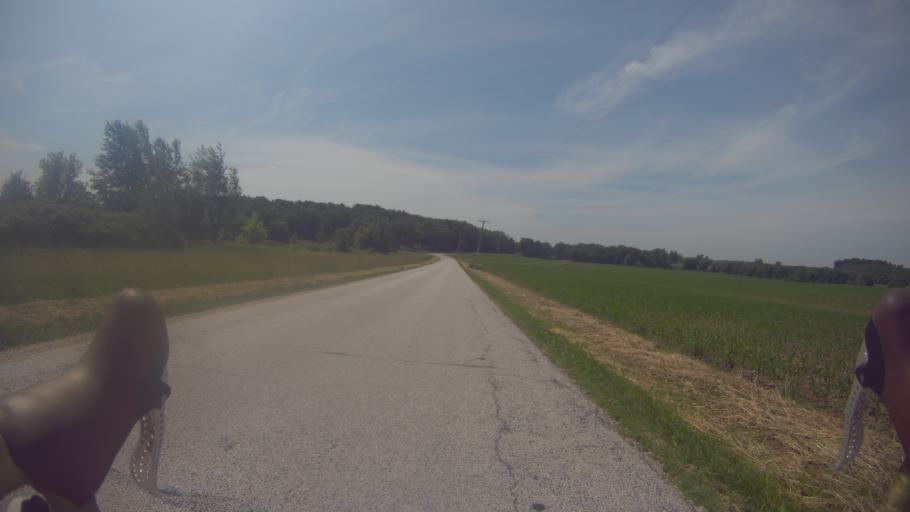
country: US
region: Wisconsin
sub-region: Jefferson County
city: Cambridge
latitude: 43.0566
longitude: -89.0213
